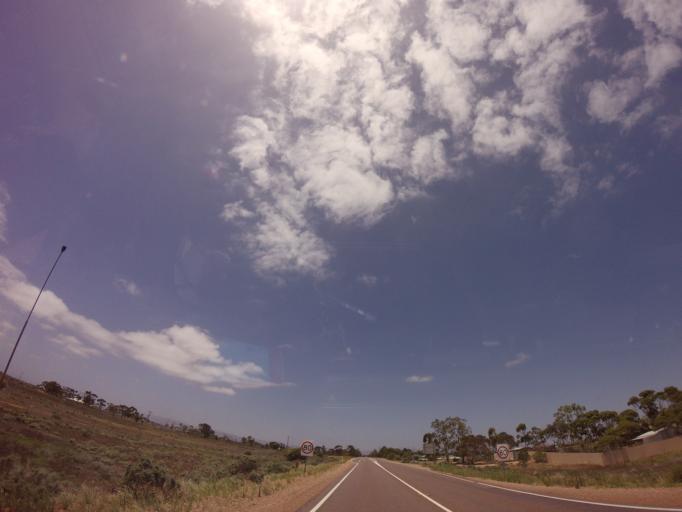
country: AU
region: South Australia
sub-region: Port Augusta
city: Port Augusta West
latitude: -32.4831
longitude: 137.7333
